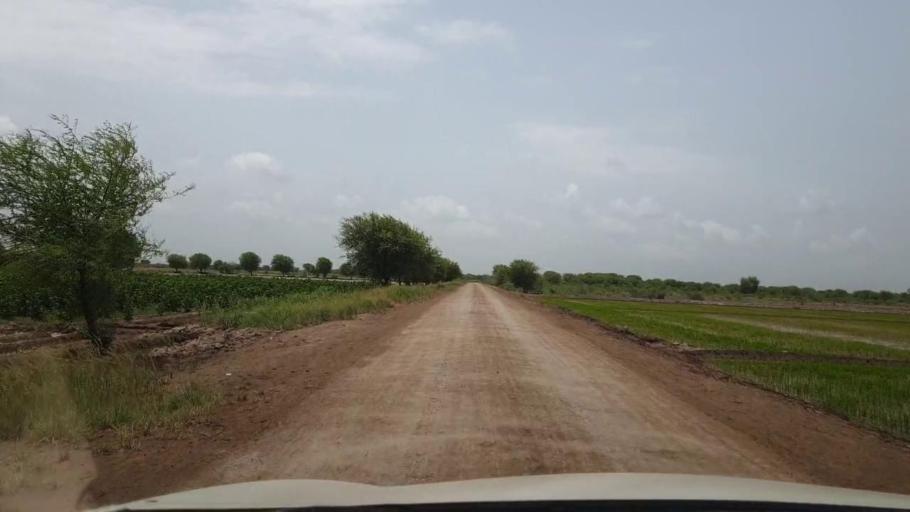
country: PK
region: Sindh
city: Chambar
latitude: 25.2125
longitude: 68.7695
